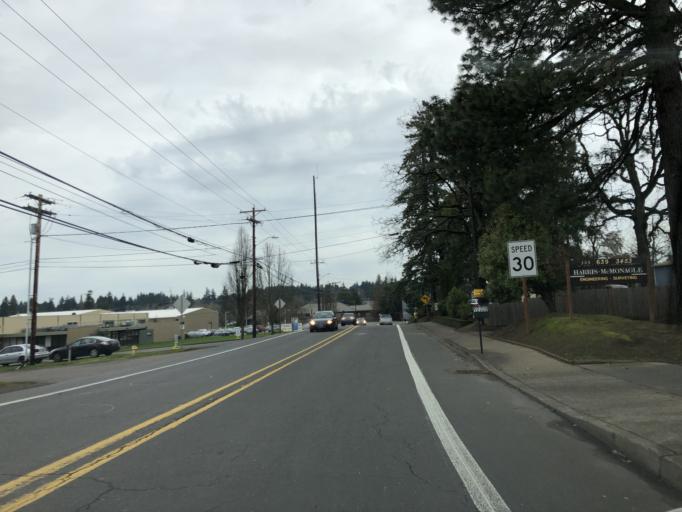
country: US
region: Oregon
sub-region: Washington County
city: Tigard
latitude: 45.4294
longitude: -122.7648
